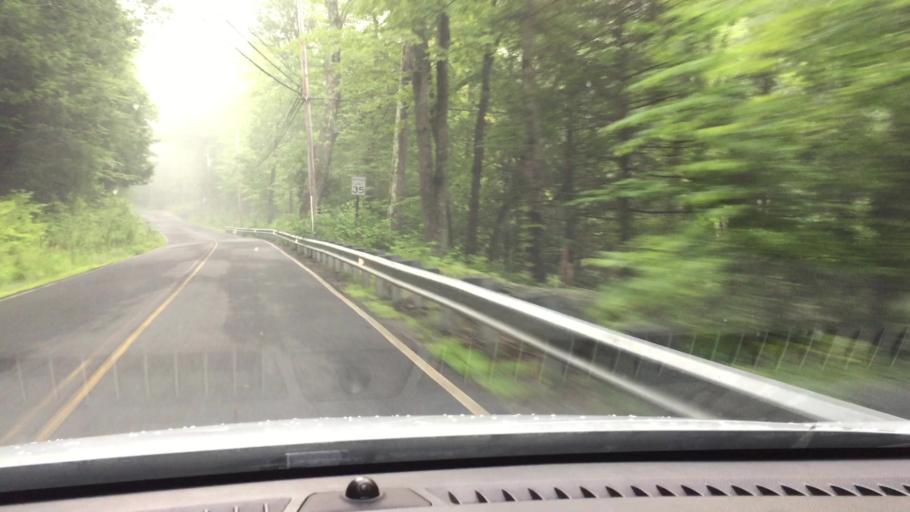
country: US
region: Massachusetts
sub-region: Hampshire County
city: Westhampton
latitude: 42.2544
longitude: -72.9307
